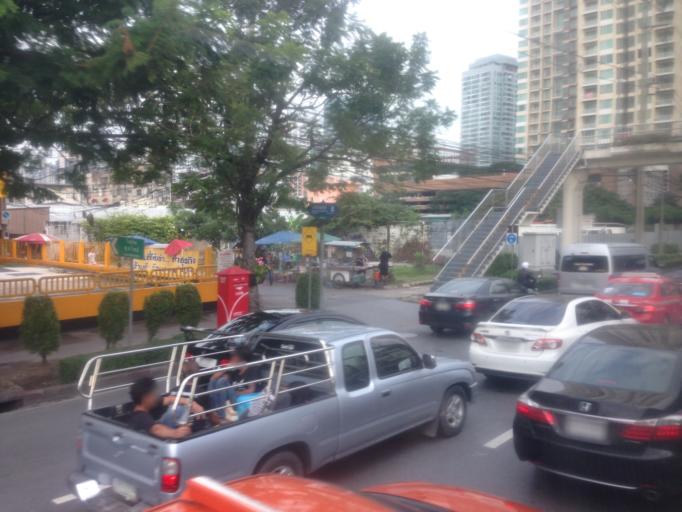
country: TH
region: Bangkok
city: Sathon
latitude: 13.7176
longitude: 100.5322
